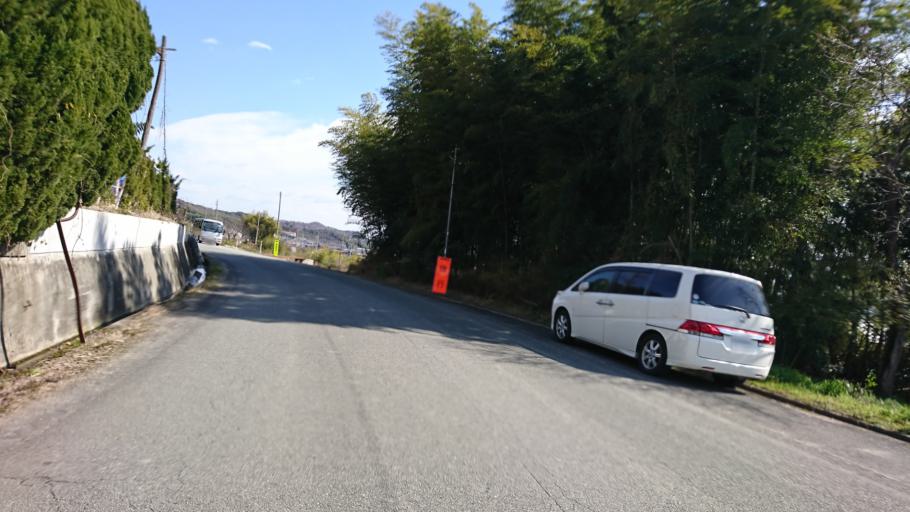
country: JP
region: Hyogo
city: Kakogawacho-honmachi
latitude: 34.8268
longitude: 134.8128
